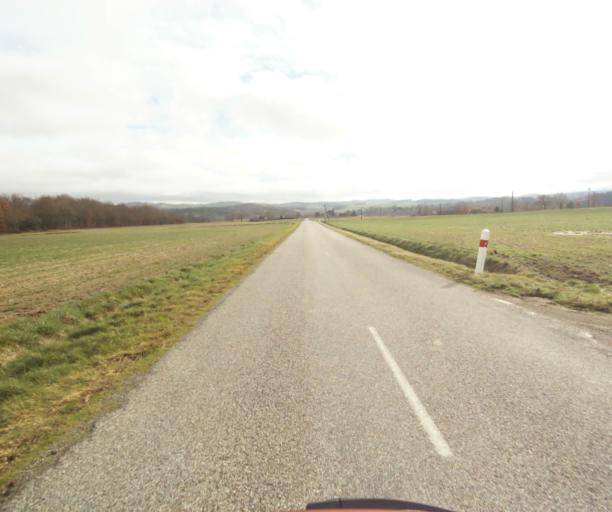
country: FR
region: Midi-Pyrenees
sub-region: Departement de l'Ariege
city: Pamiers
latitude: 43.1088
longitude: 1.5329
